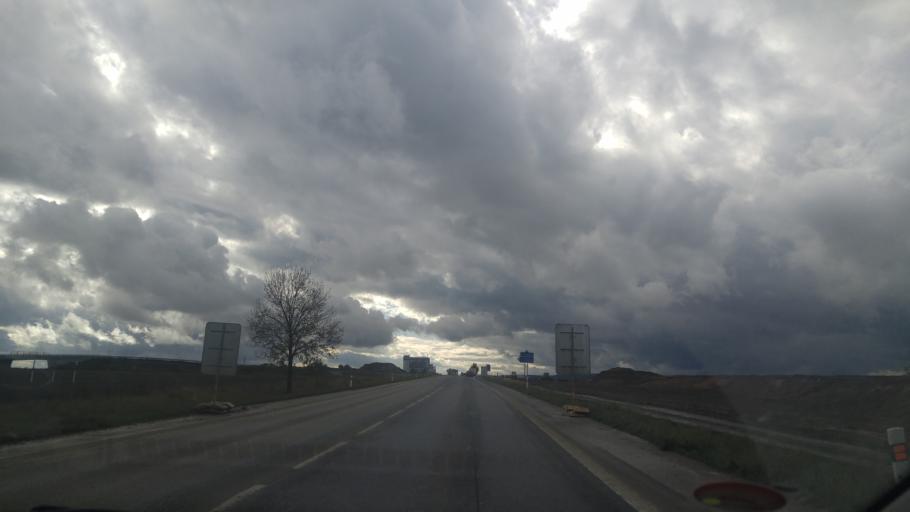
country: CZ
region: Jihocesky
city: Dolni Bukovsko
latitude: 49.1561
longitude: 14.6370
